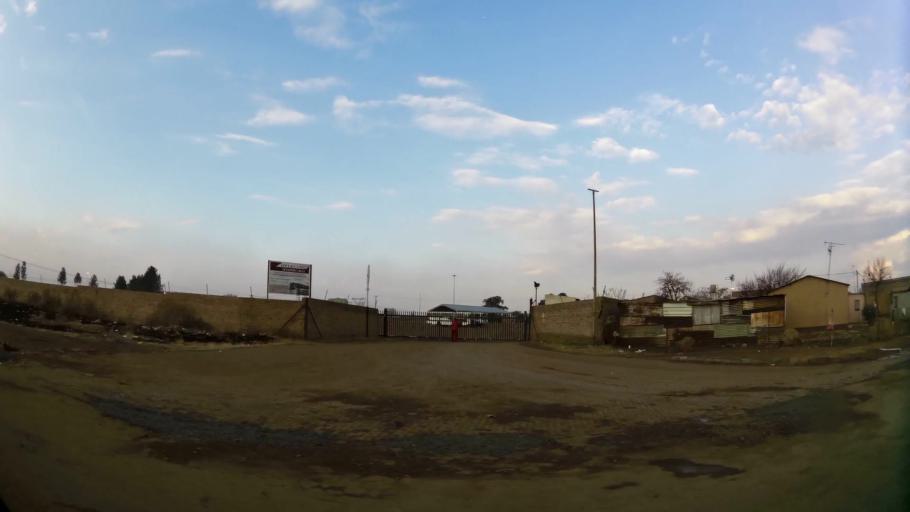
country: ZA
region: Gauteng
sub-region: City of Johannesburg Metropolitan Municipality
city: Orange Farm
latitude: -26.5563
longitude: 27.8304
